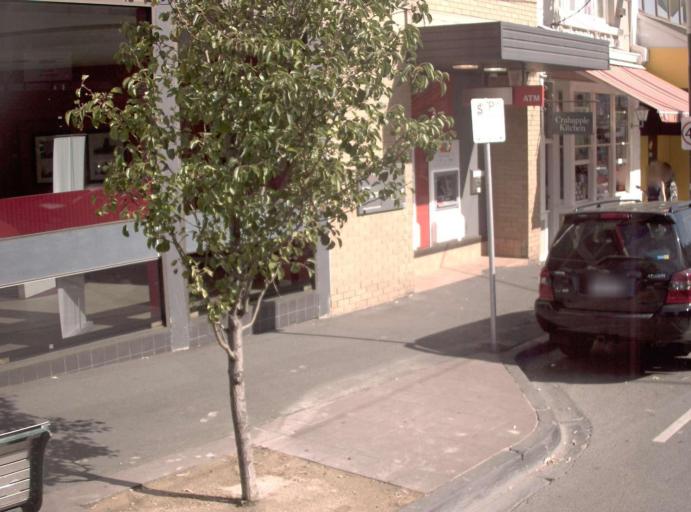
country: AU
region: Victoria
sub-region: Boroondara
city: Hawthorn East
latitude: -37.8212
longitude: 145.0356
